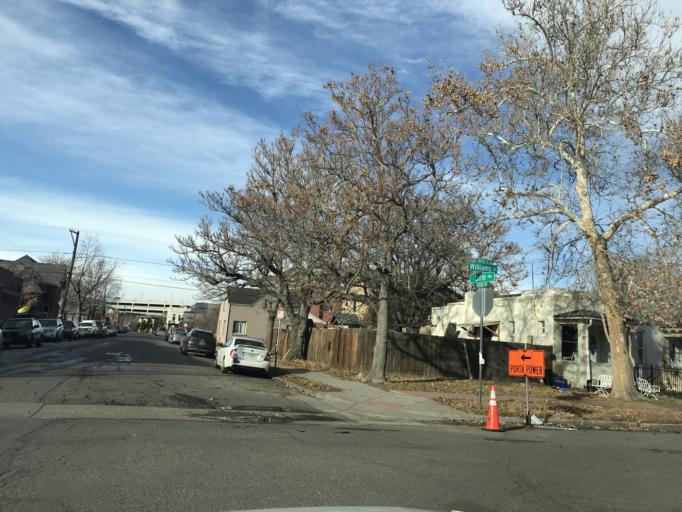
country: US
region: Colorado
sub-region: Denver County
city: Denver
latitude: 39.7701
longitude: -104.9659
